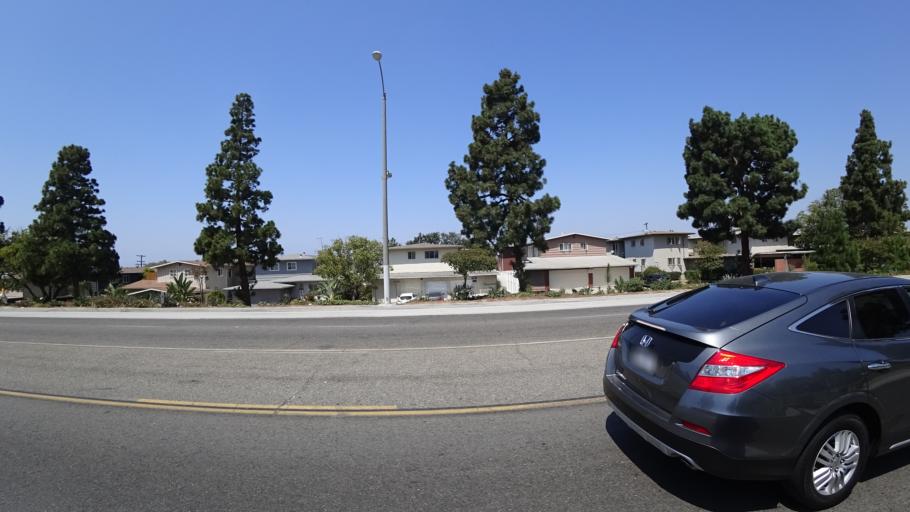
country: US
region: California
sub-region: Los Angeles County
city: Westmont
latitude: 33.9481
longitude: -118.3264
